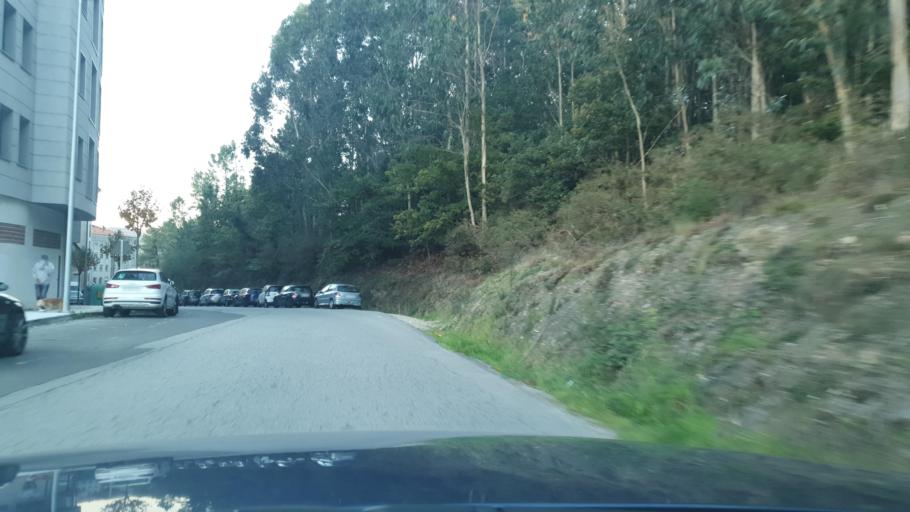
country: ES
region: Galicia
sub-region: Provincia da Coruna
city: Santiago de Compostela
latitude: 42.8460
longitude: -8.5739
